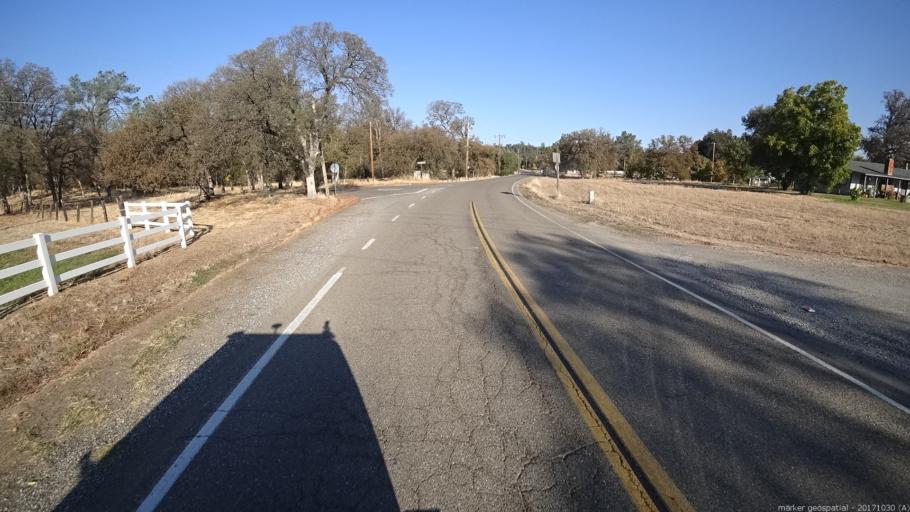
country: US
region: California
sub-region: Shasta County
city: Palo Cedro
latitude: 40.5637
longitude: -122.1909
